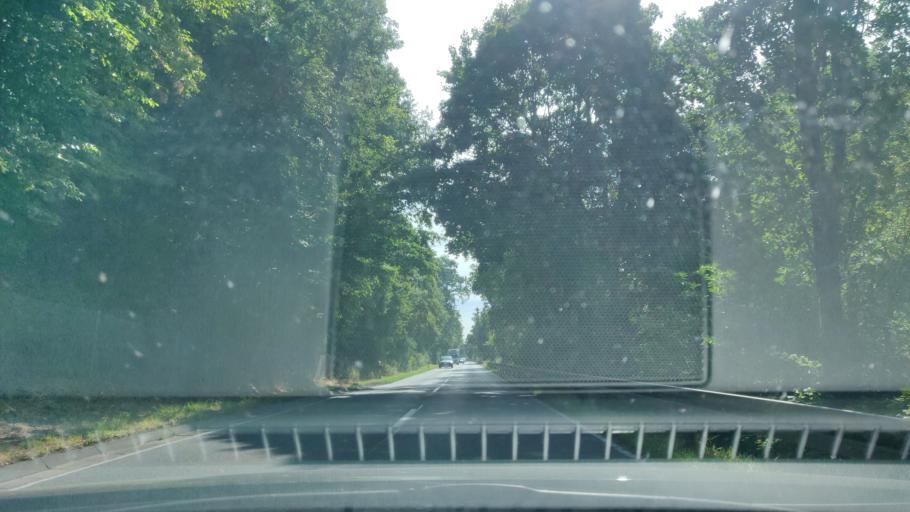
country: DE
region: Hesse
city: Fritzlar
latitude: 51.1306
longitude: 9.2155
